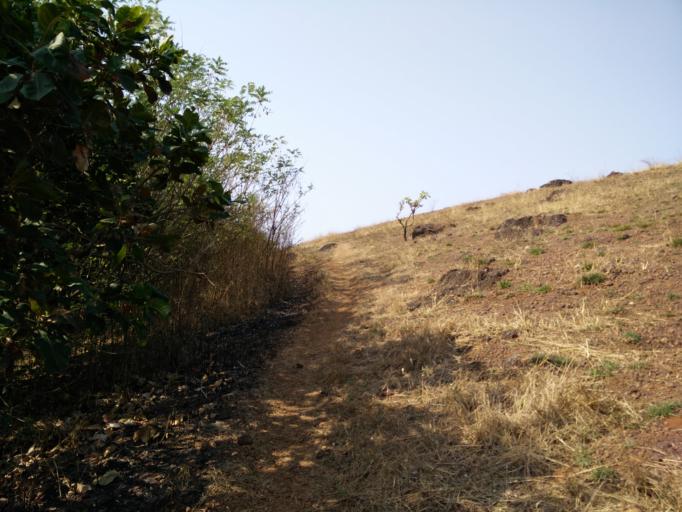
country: IN
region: Goa
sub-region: North Goa
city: Candolim
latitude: 15.4942
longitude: 73.7698
